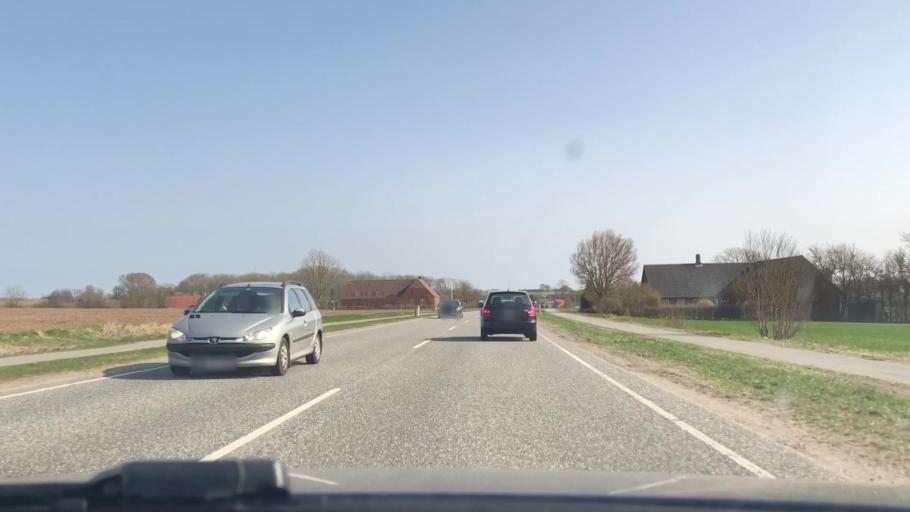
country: DK
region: South Denmark
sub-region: Sonderborg Kommune
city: Guderup
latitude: 54.9729
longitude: 9.8946
